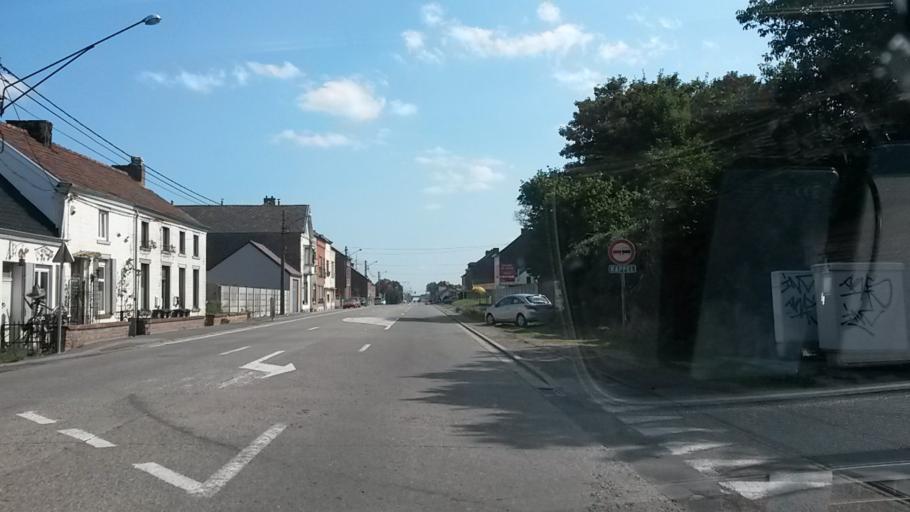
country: BE
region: Wallonia
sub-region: Province du Hainaut
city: Anderlues
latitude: 50.4059
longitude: 4.2766
